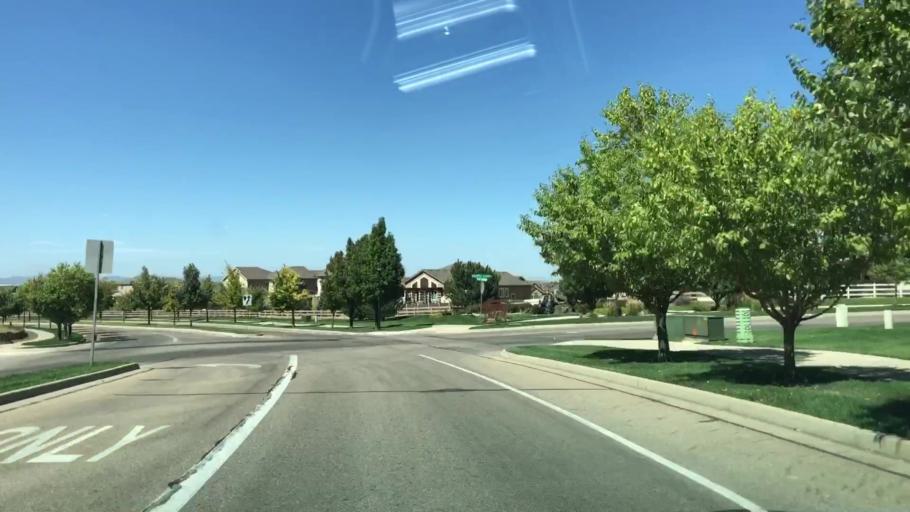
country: US
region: Colorado
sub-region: Weld County
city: Windsor
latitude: 40.4414
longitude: -104.9678
